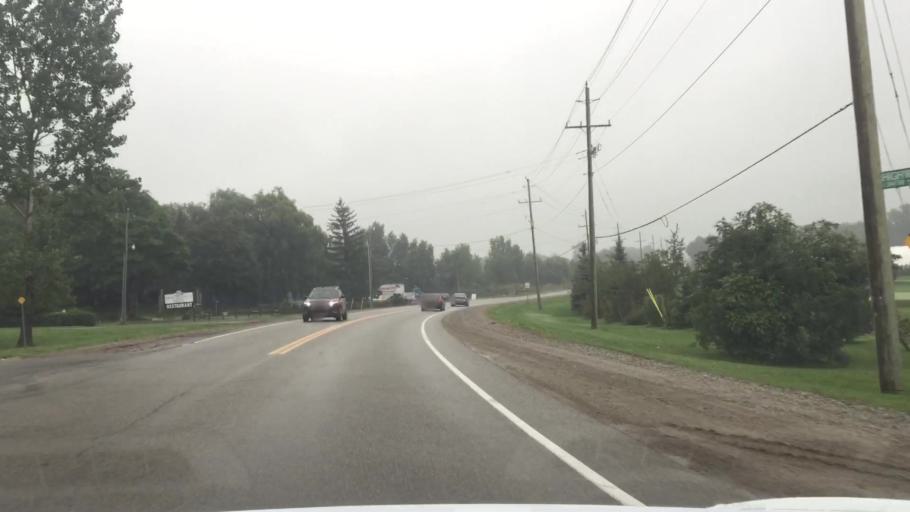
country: CA
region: Ontario
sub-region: Oxford County
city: Woodstock
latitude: 43.1055
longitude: -80.7310
